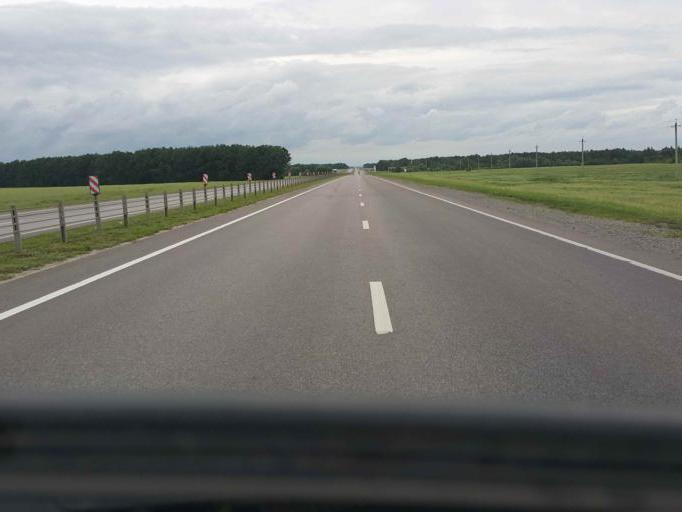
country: RU
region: Tambov
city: Zavoronezhskoye
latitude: 52.9044
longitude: 40.6472
